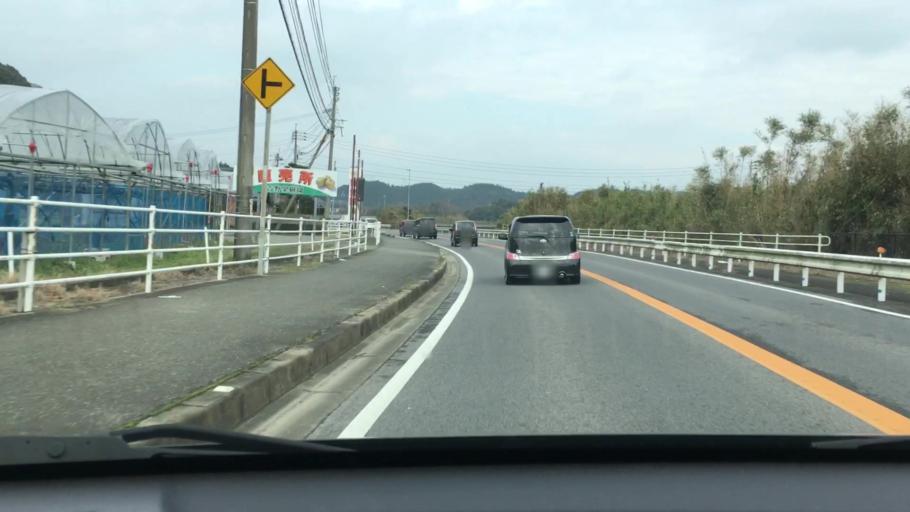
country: JP
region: Saga Prefecture
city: Imaricho-ko
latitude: 33.3262
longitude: 129.9297
